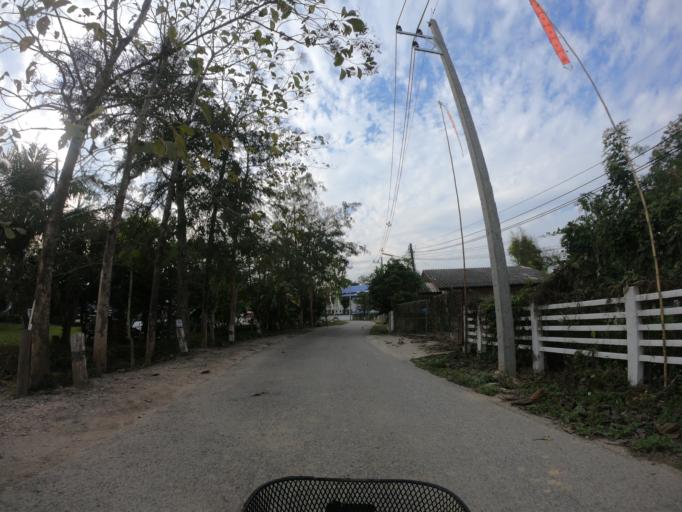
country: TH
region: Chiang Mai
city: San Sai
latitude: 18.7957
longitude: 99.0545
